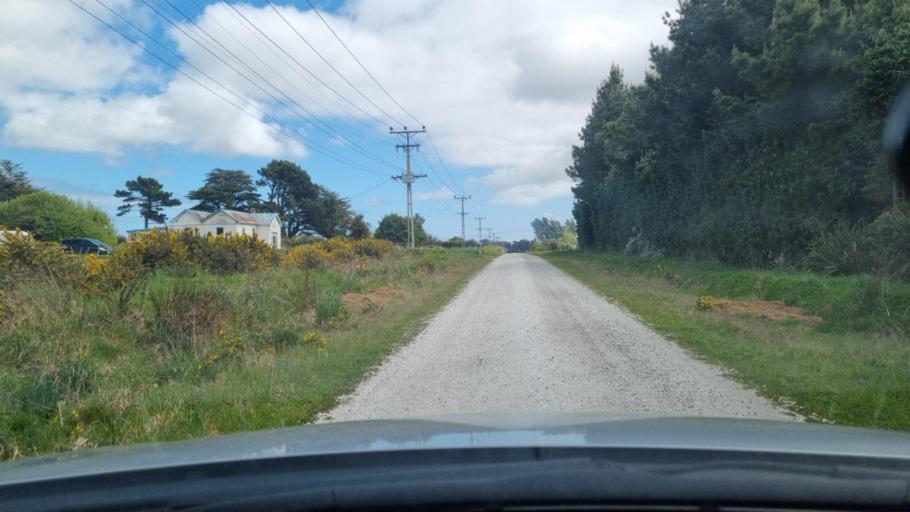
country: NZ
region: Southland
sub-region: Invercargill City
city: Invercargill
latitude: -46.4431
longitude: 168.3930
